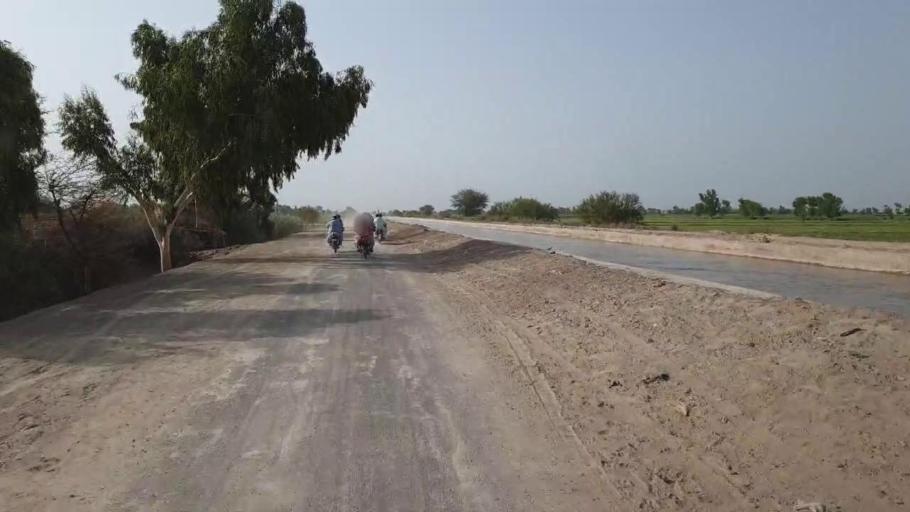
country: PK
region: Sindh
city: Daur
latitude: 26.3409
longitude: 68.1630
